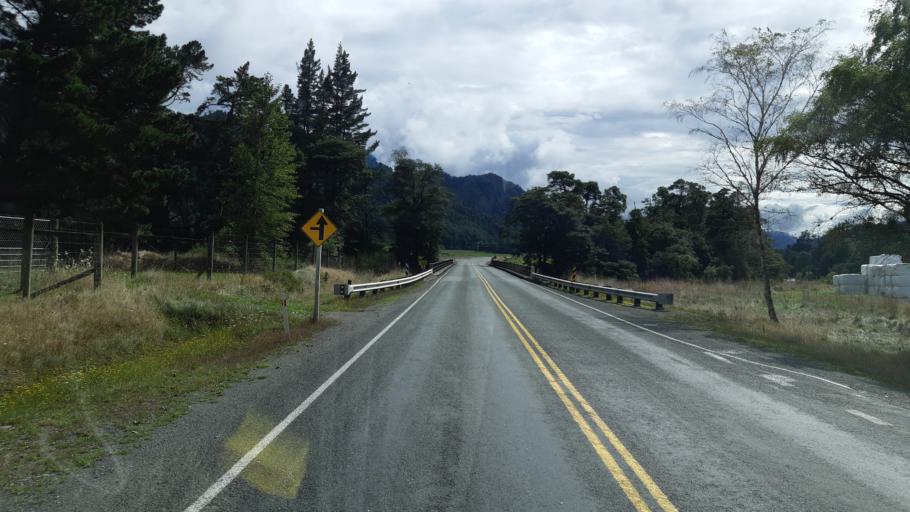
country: NZ
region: Tasman
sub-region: Tasman District
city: Wakefield
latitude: -41.7748
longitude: 172.3784
